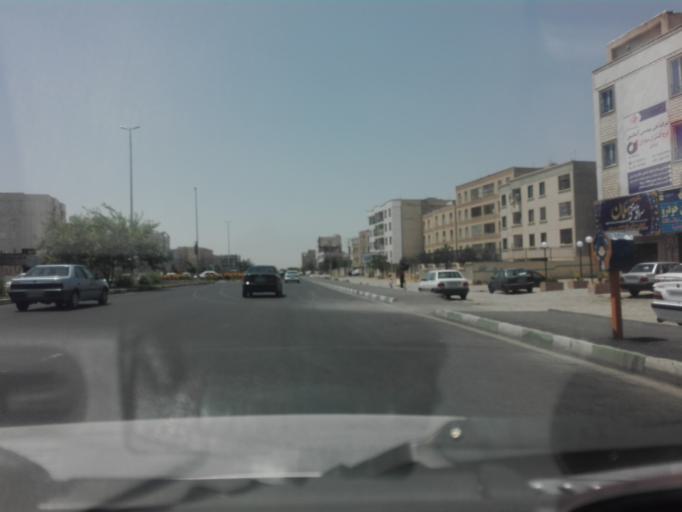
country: IR
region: Tehran
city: Malard
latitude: 35.7108
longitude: 50.9800
